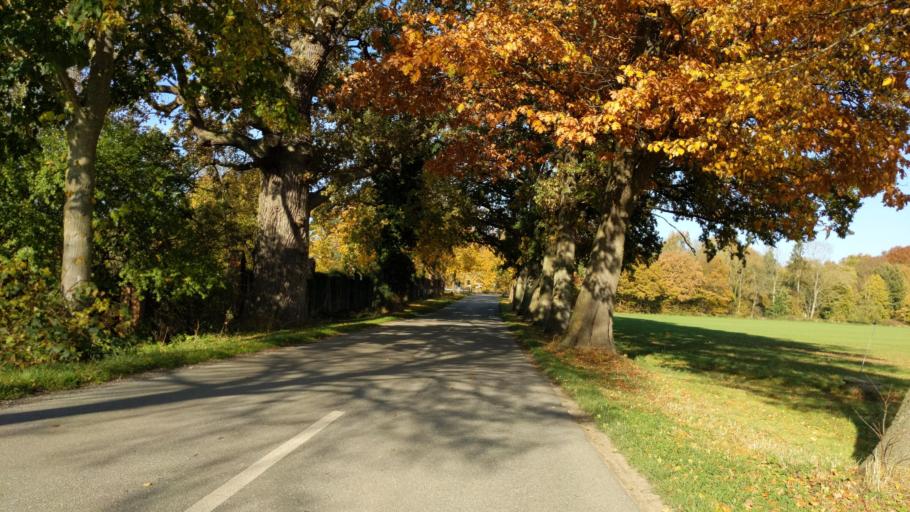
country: DE
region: Schleswig-Holstein
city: Neustadt in Holstein
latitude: 54.1272
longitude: 10.7775
